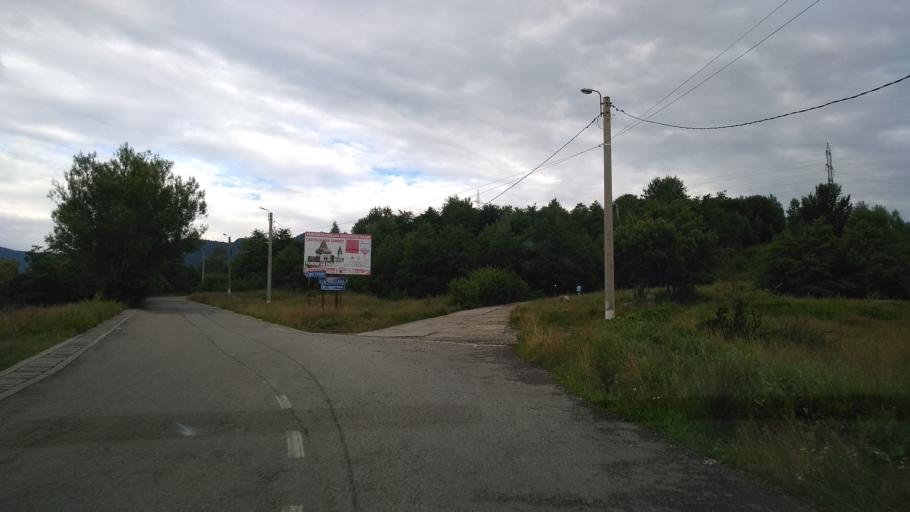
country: RO
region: Hunedoara
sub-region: Municipiul  Vulcan
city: Jiu-Paroseni
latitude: 45.3650
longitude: 23.2843
